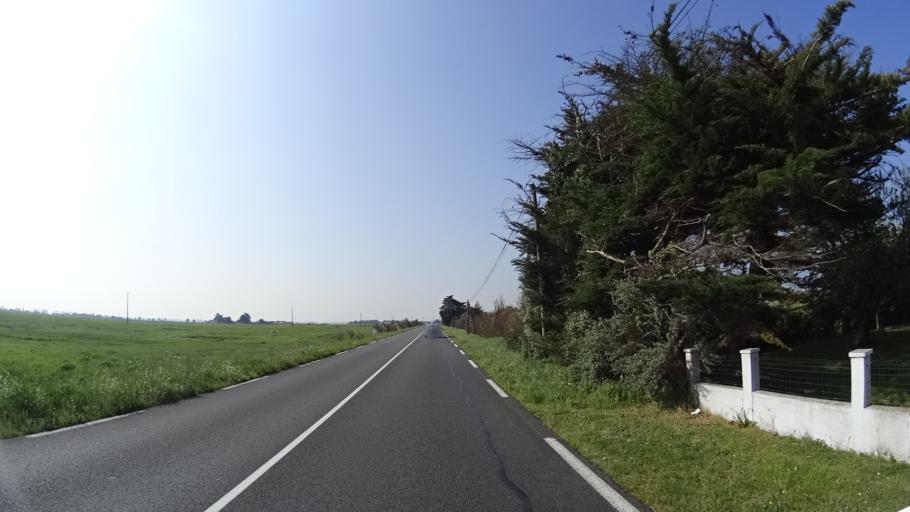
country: FR
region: Pays de la Loire
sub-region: Departement de la Vendee
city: Bouin
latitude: 46.9842
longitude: -1.9830
